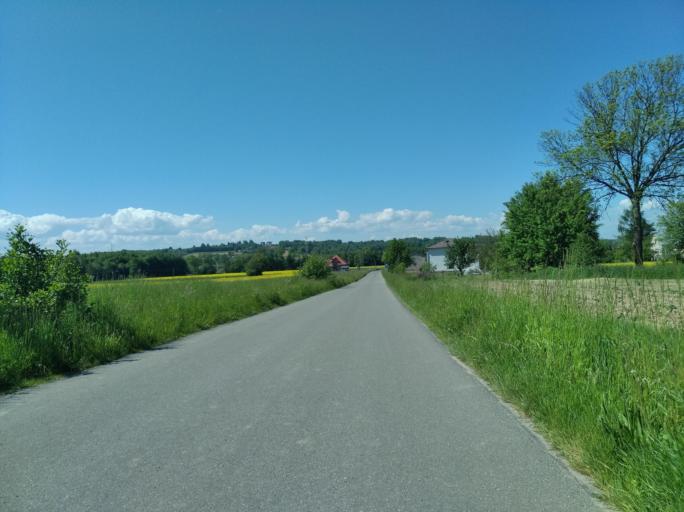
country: PL
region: Subcarpathian Voivodeship
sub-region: Powiat krosnienski
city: Korczyna
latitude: 49.7213
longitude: 21.7798
